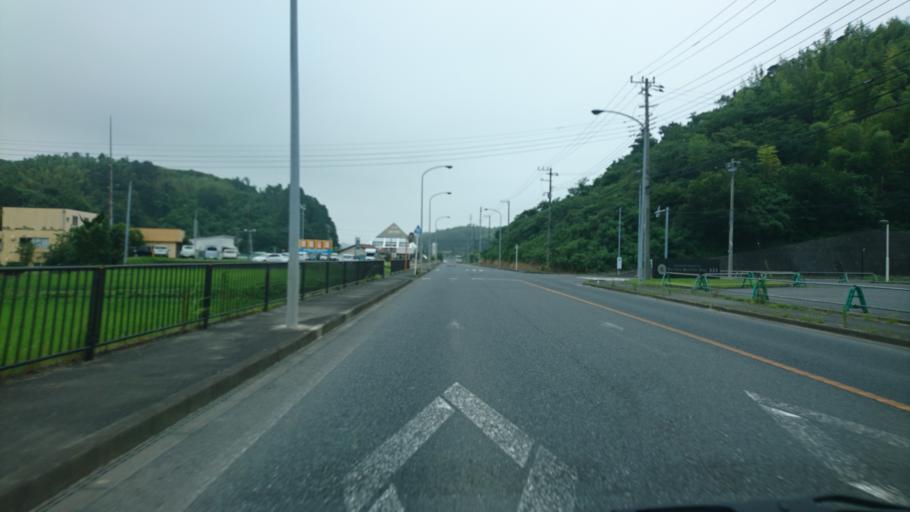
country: JP
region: Chiba
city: Kimitsu
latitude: 35.2734
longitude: 139.9012
